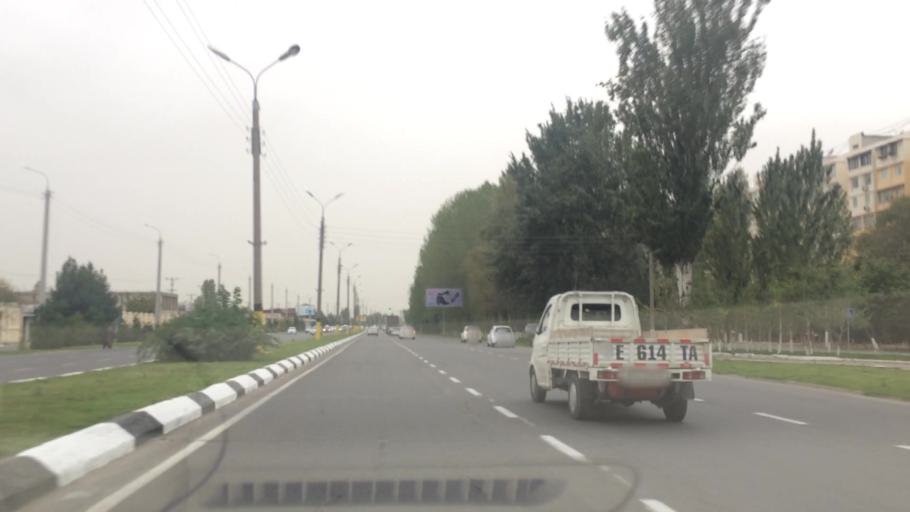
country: UZ
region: Toshkent
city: Salor
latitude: 41.3186
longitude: 69.3584
